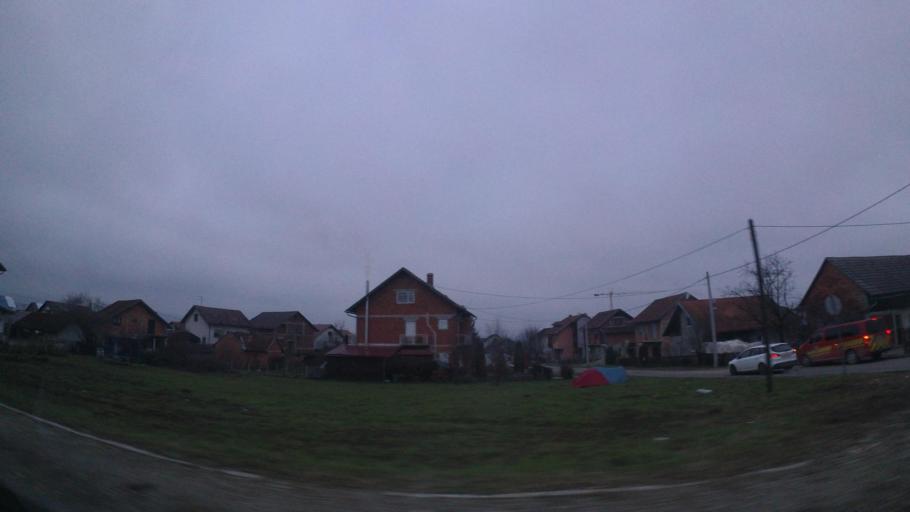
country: HR
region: Sisacko-Moslavacka
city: Petrinja
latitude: 45.4372
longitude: 16.2998
